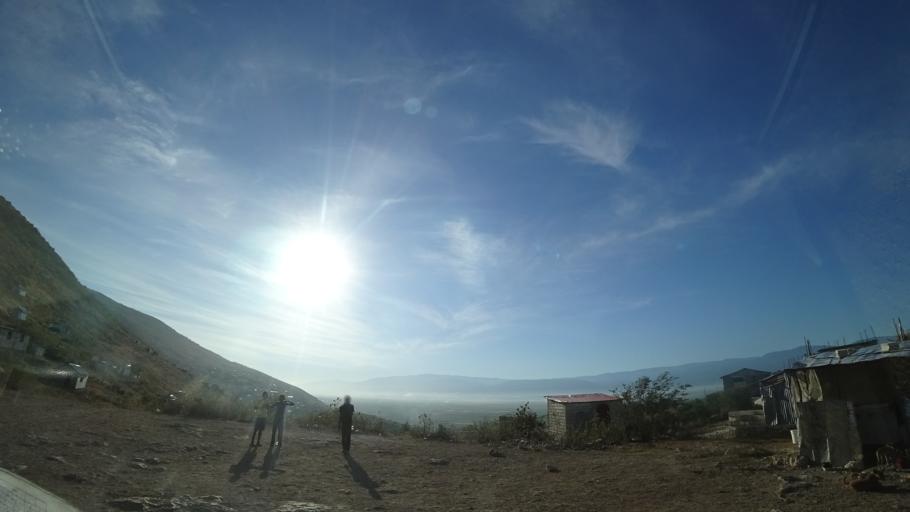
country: HT
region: Ouest
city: Croix des Bouquets
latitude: 18.6699
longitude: -72.2253
